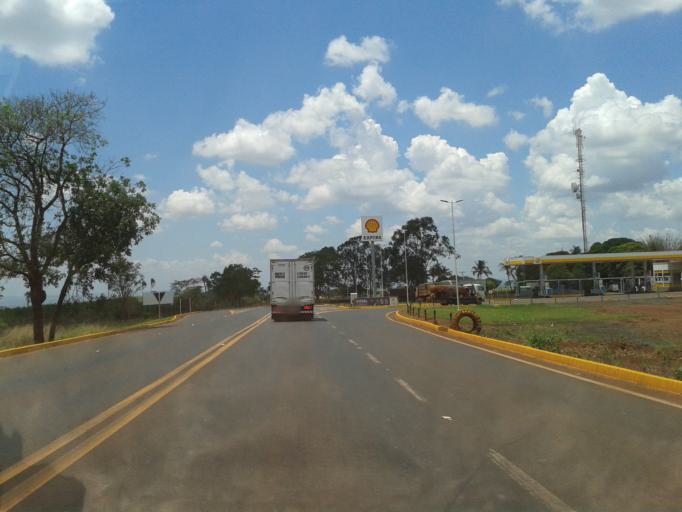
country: BR
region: Goias
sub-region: Itumbiara
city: Itumbiara
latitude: -18.3872
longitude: -49.3403
